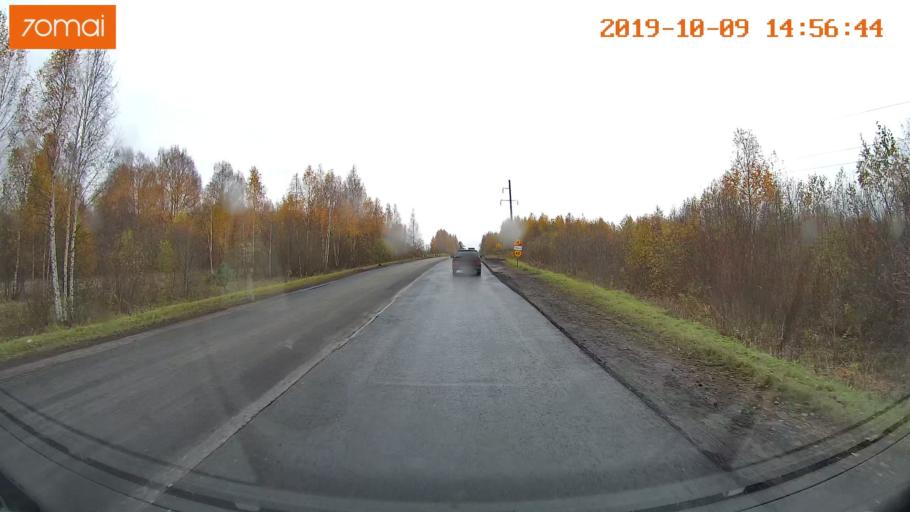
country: RU
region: Kostroma
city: Chistyye Bory
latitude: 58.3436
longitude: 41.6483
